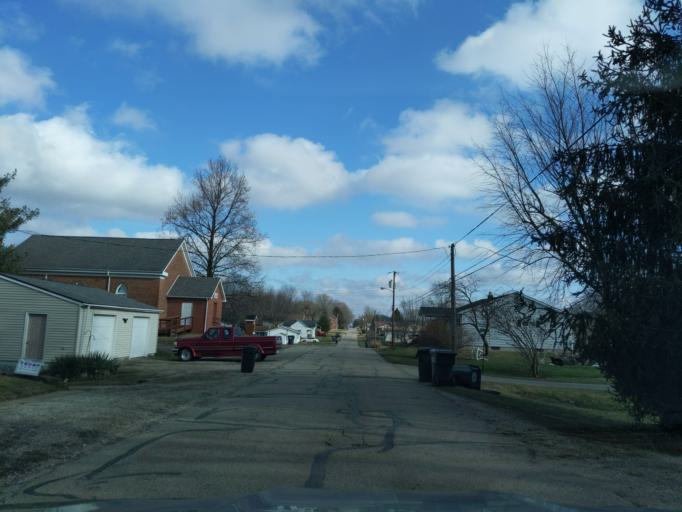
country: US
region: Indiana
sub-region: Ripley County
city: Batesville
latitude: 39.3093
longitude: -85.3298
